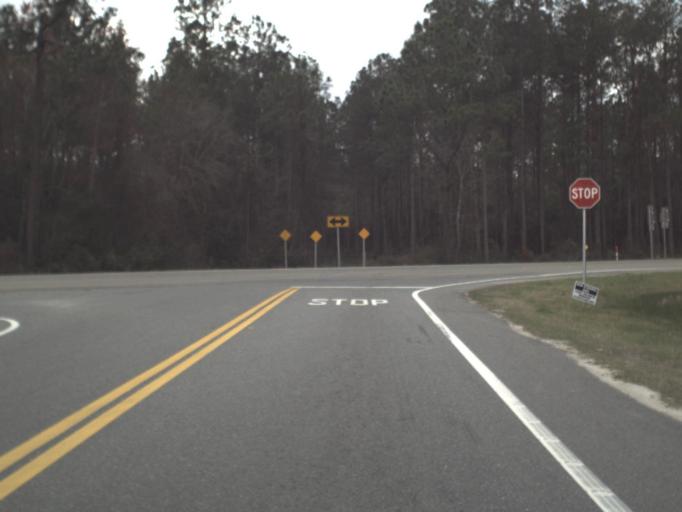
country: US
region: Florida
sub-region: Gadsden County
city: Quincy
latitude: 30.3887
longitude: -84.6845
